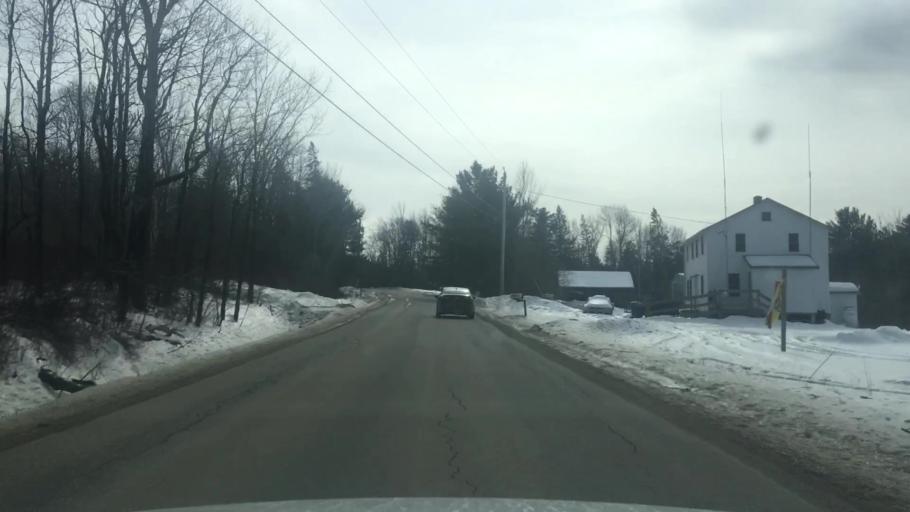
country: US
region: Maine
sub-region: Hancock County
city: Orland
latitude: 44.5869
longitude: -68.7259
